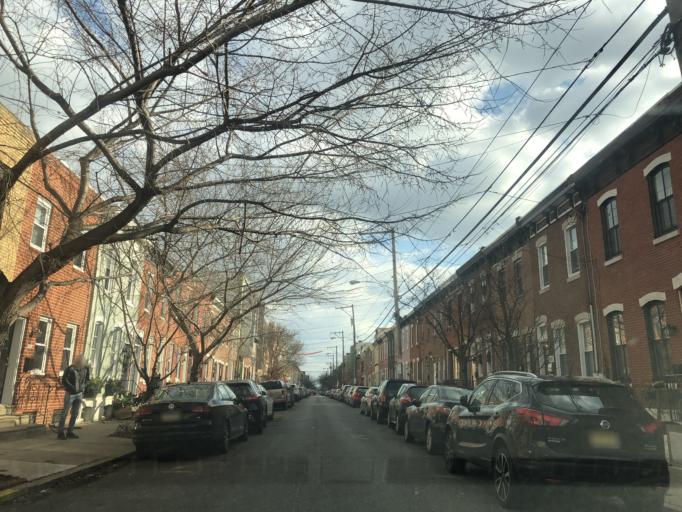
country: US
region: Pennsylvania
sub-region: Philadelphia County
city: Philadelphia
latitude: 39.9405
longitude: -75.1779
